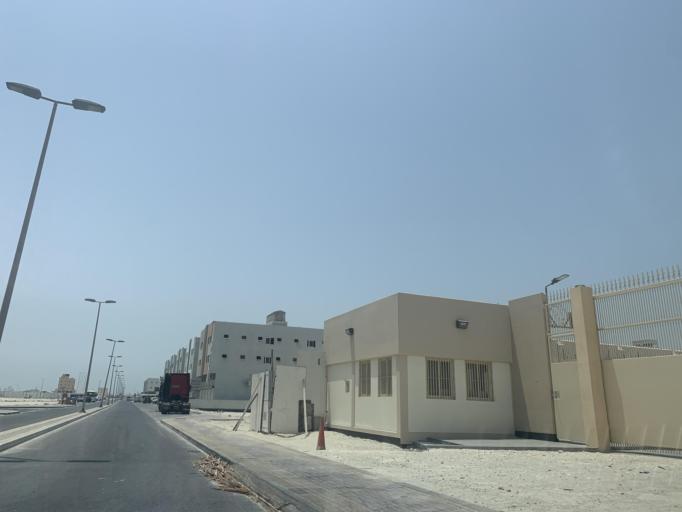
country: BH
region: Muharraq
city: Al Hadd
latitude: 26.2596
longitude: 50.6719
